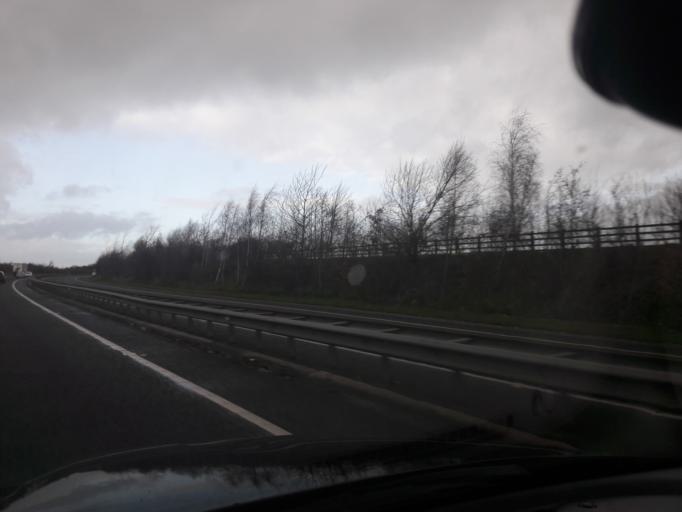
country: IE
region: Leinster
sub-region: An Mhi
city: Ashbourne
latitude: 53.4927
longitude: -6.4111
